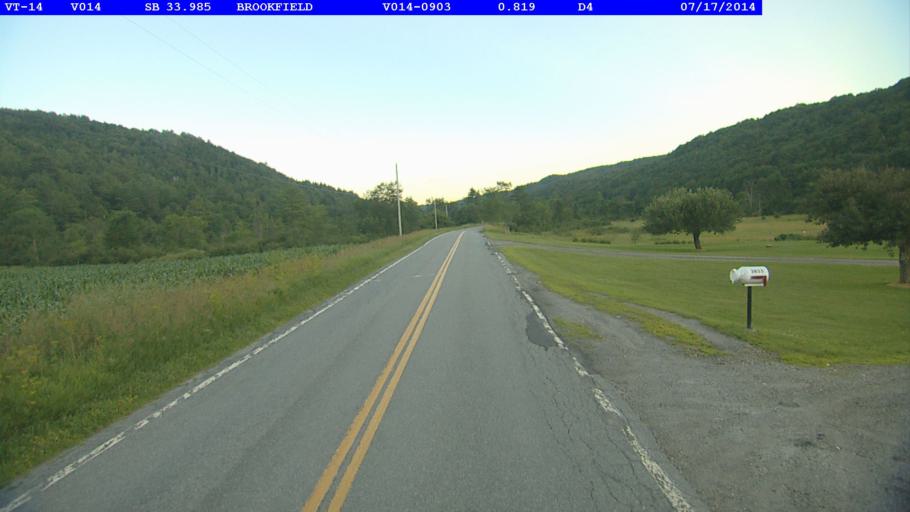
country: US
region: Vermont
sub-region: Orange County
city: Chelsea
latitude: 43.9908
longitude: -72.5560
